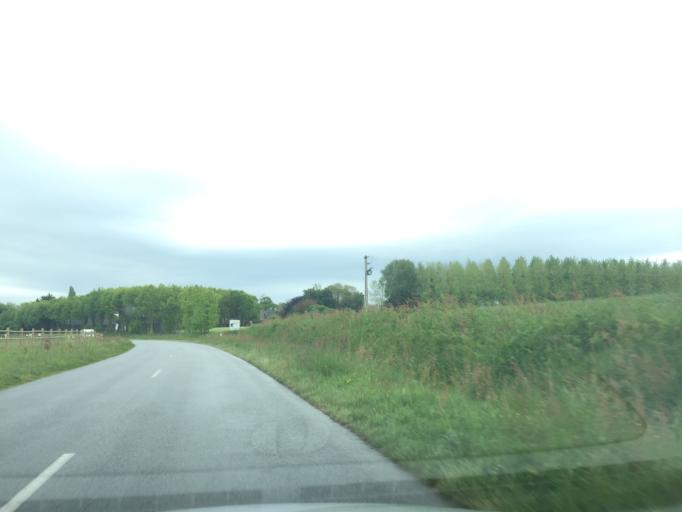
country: FR
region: Brittany
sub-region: Departement des Cotes-d'Armor
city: Crehen
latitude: 48.5548
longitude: -2.2390
